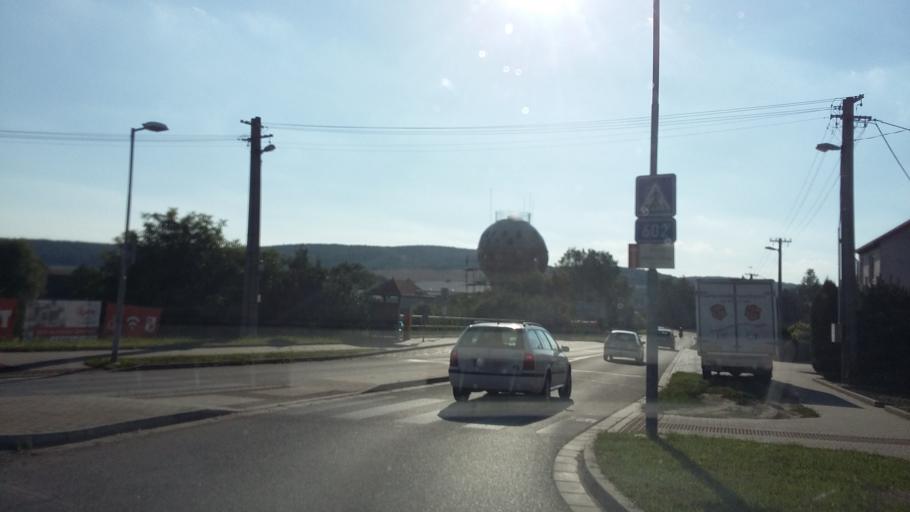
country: CZ
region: South Moravian
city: Troubsko
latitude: 49.1769
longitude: 16.5043
